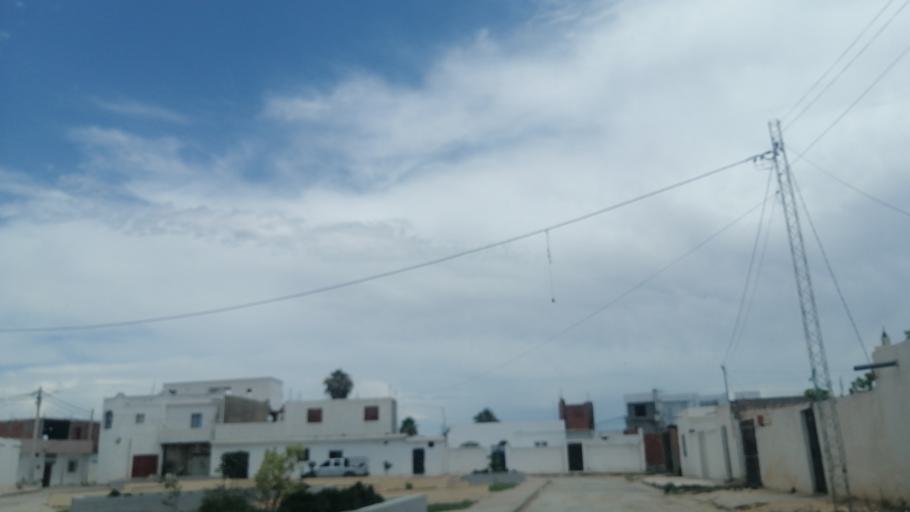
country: TN
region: Al Qayrawan
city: Sbikha
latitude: 36.1264
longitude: 10.0915
